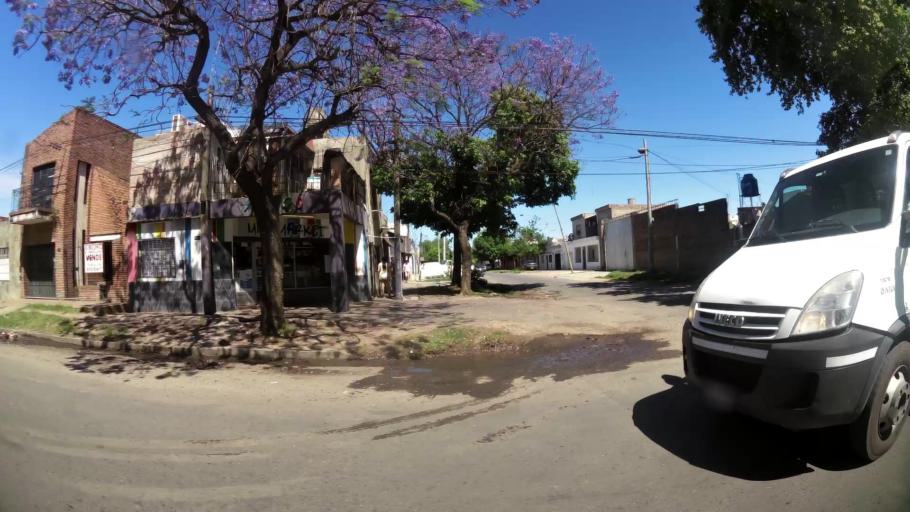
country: AR
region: Santa Fe
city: Perez
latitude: -32.9640
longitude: -60.7117
